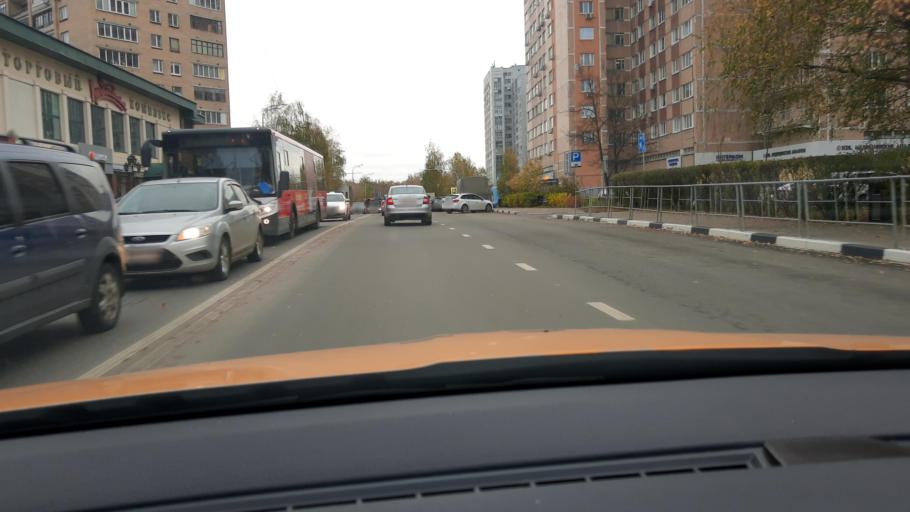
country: RU
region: Moskovskaya
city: Odintsovo
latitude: 55.6809
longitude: 37.2653
